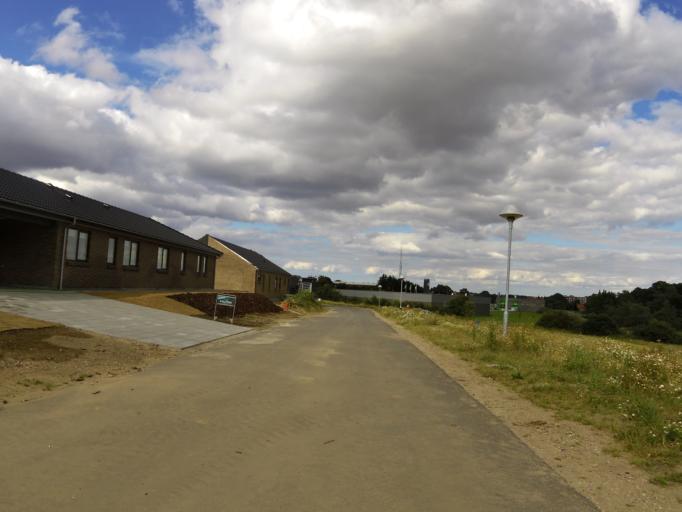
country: DK
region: South Denmark
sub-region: Haderslev Kommune
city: Haderslev
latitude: 55.2346
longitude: 9.4838
